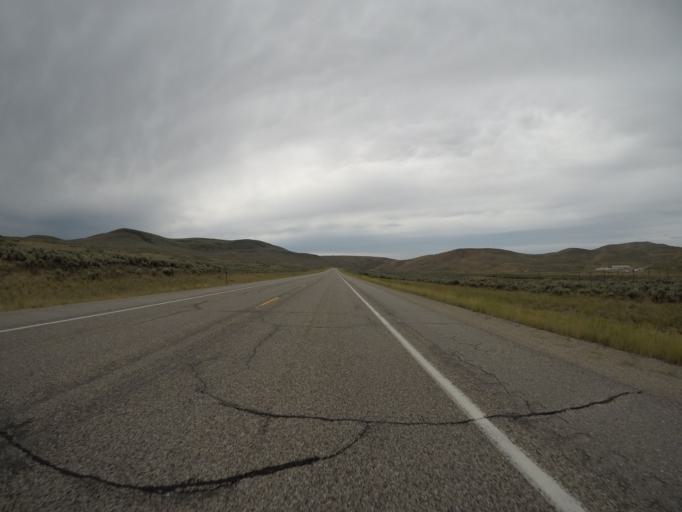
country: US
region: Wyoming
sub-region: Lincoln County
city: Kemmerer
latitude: 41.8172
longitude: -110.7845
